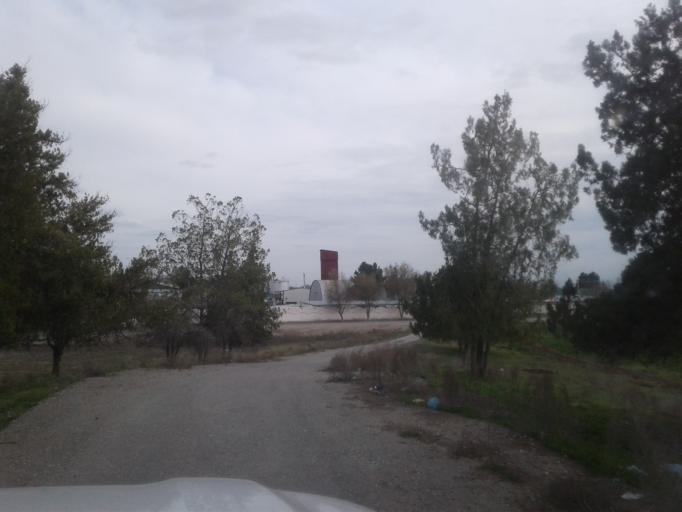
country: TM
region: Ahal
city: Abadan
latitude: 38.1239
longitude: 58.3449
